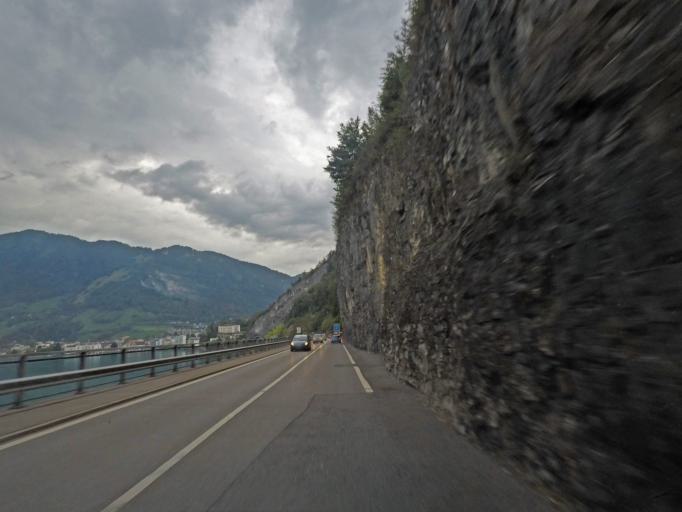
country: CH
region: Schwyz
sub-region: Bezirk Schwyz
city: Ingenbohl
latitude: 46.9857
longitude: 8.6121
